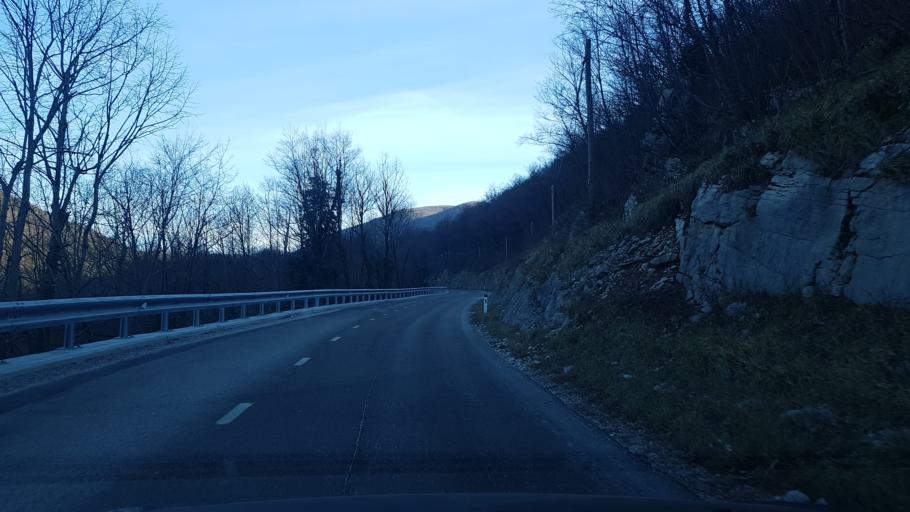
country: SI
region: Nova Gorica
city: Kromberk
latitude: 46.0080
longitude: 13.6953
